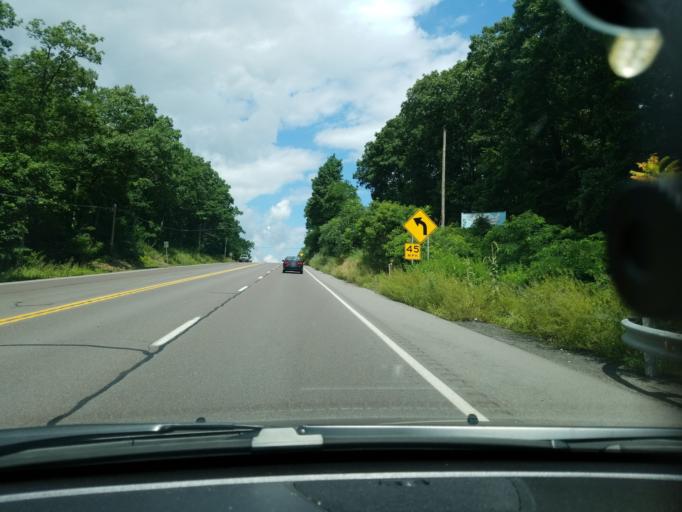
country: US
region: Pennsylvania
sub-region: Northumberland County
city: Elysburg
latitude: 40.8465
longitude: -76.5225
